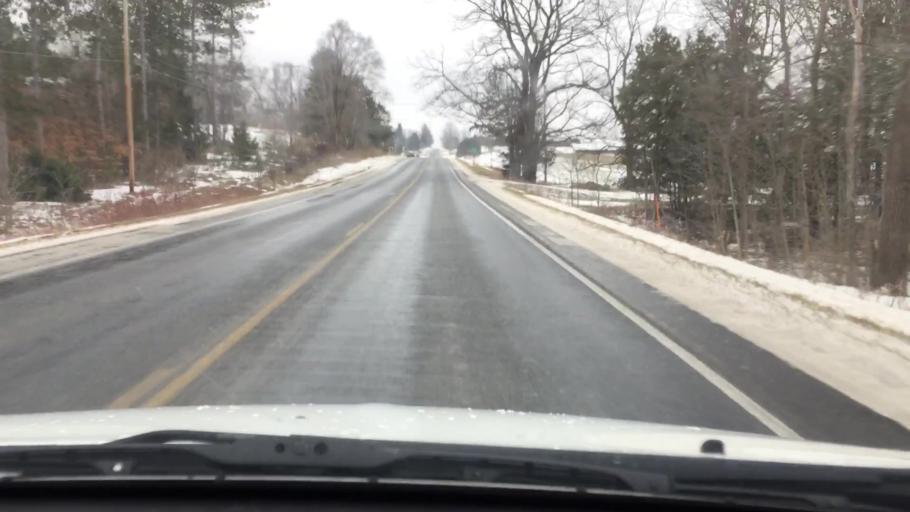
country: US
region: Michigan
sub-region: Wexford County
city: Cadillac
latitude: 44.0760
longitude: -85.4441
